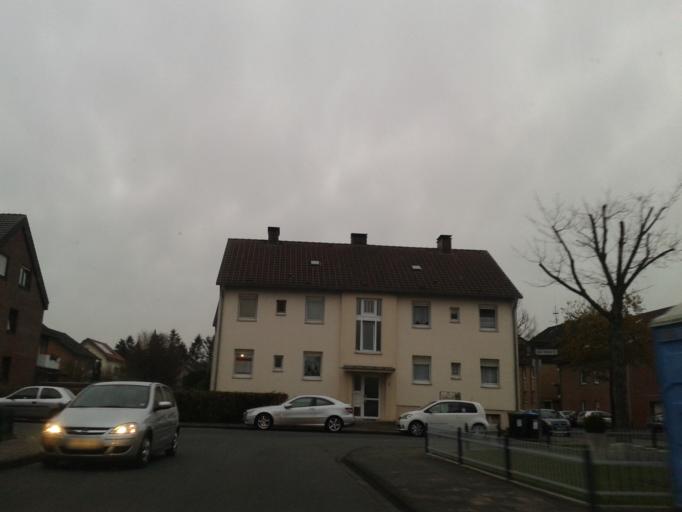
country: DE
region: North Rhine-Westphalia
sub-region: Regierungsbezirk Detmold
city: Paderborn
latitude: 51.7565
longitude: 8.7247
